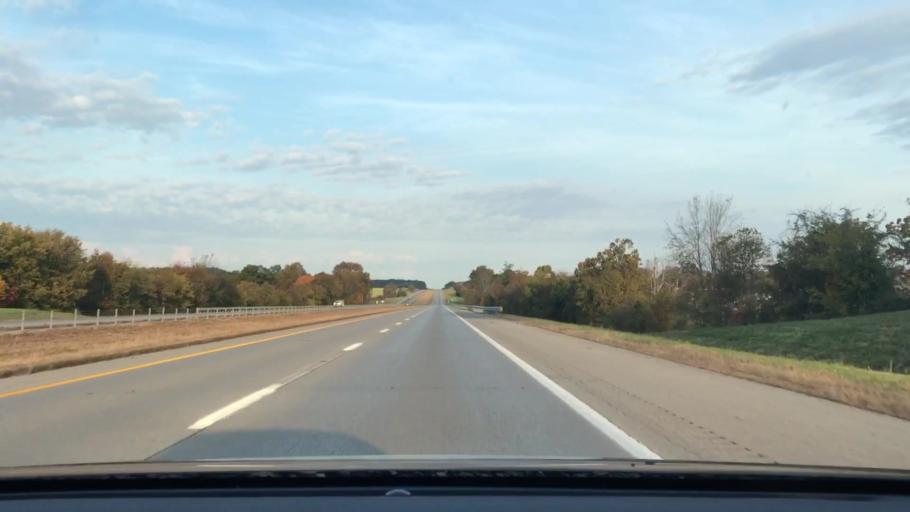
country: US
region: Kentucky
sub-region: Christian County
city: Hopkinsville
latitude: 36.7606
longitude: -87.5390
